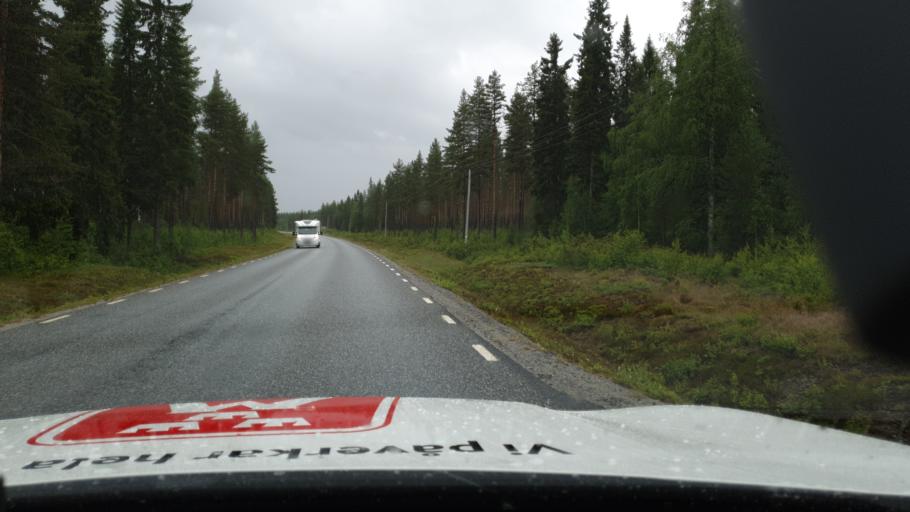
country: SE
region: Vaesterbotten
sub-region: Vilhelmina Kommun
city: Vilhelmina
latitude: 64.3791
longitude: 16.9001
